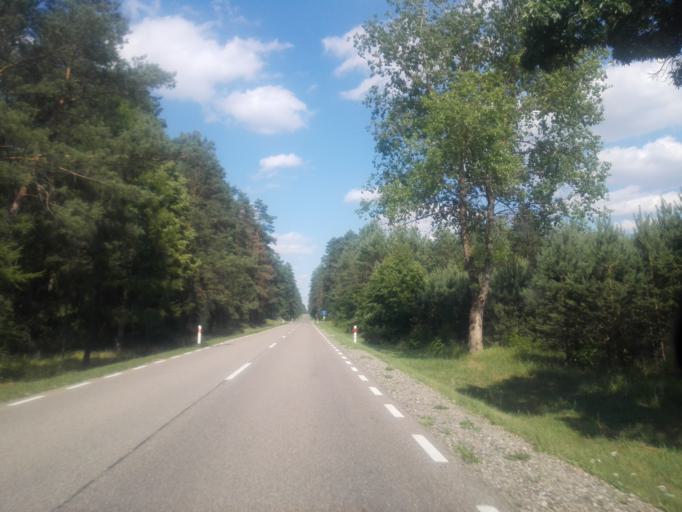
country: PL
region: Podlasie
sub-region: Powiat sejnenski
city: Krasnopol
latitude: 53.9588
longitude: 23.2239
